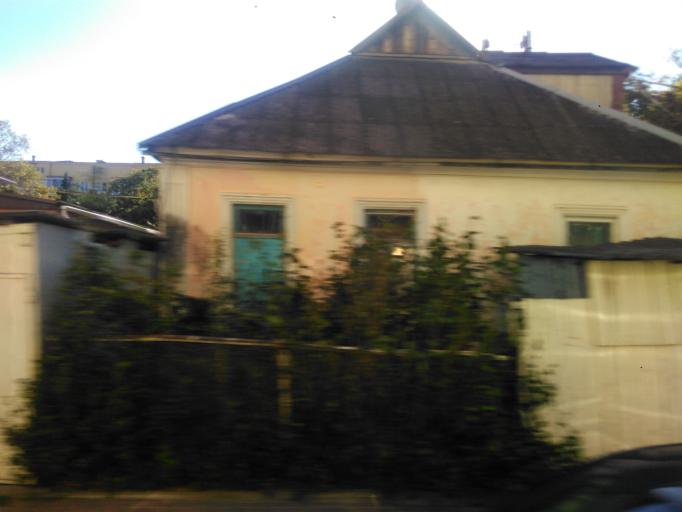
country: RU
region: Krasnodarskiy
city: Gelendzhik
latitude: 44.5546
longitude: 38.0755
